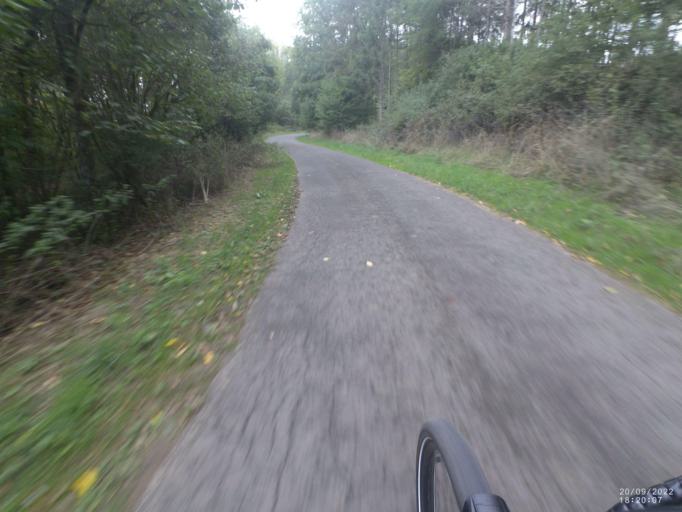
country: DE
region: Rheinland-Pfalz
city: Demerath
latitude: 50.1669
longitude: 6.9444
